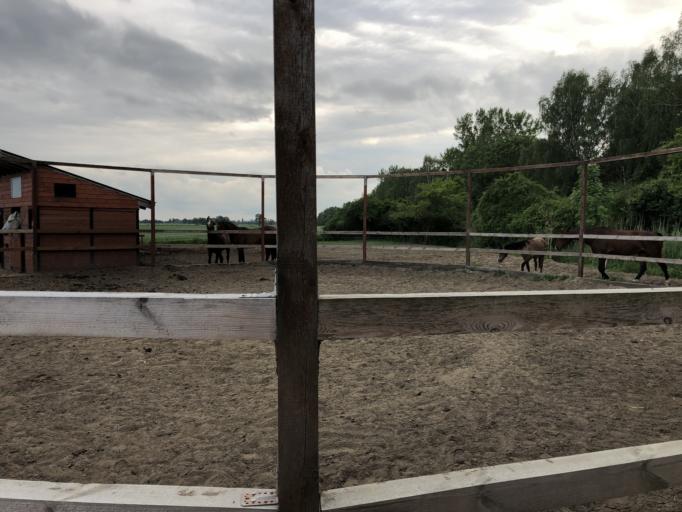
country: PL
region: Pomeranian Voivodeship
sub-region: Powiat gdanski
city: Suchy Dab
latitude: 54.2896
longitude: 18.7599
